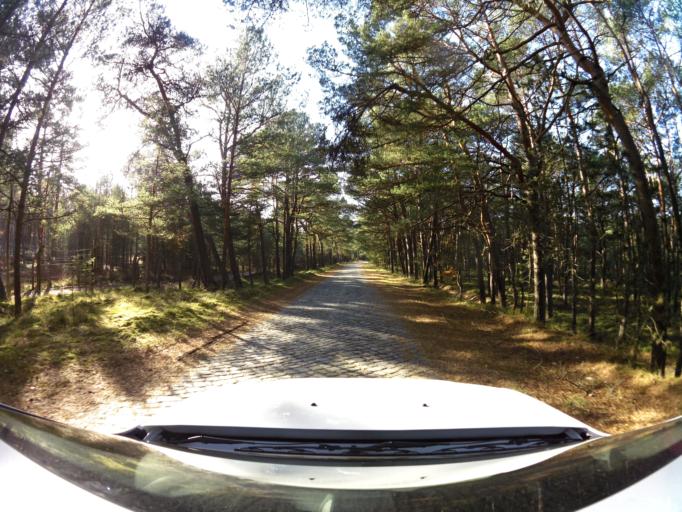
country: PL
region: West Pomeranian Voivodeship
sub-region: Powiat gryficki
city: Trzebiatow
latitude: 54.1176
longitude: 15.1776
